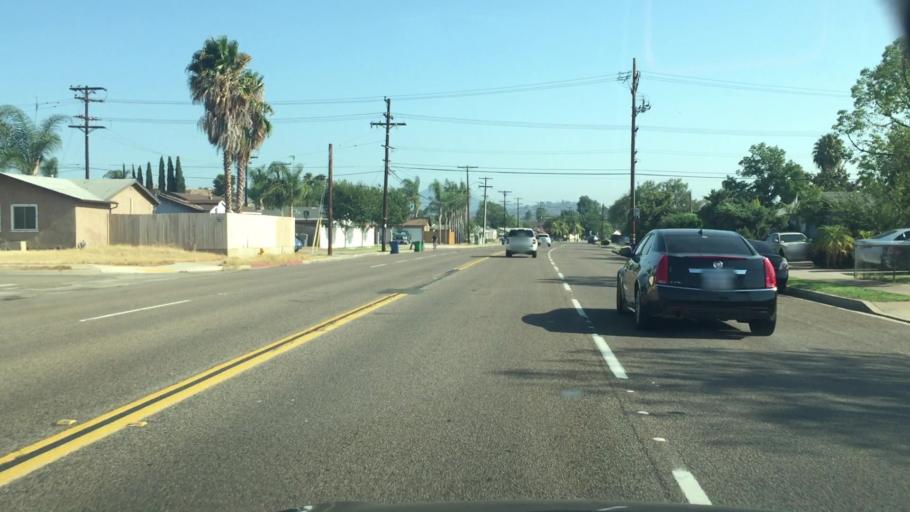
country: US
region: California
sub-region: San Diego County
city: Bostonia
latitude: 32.8175
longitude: -116.9497
